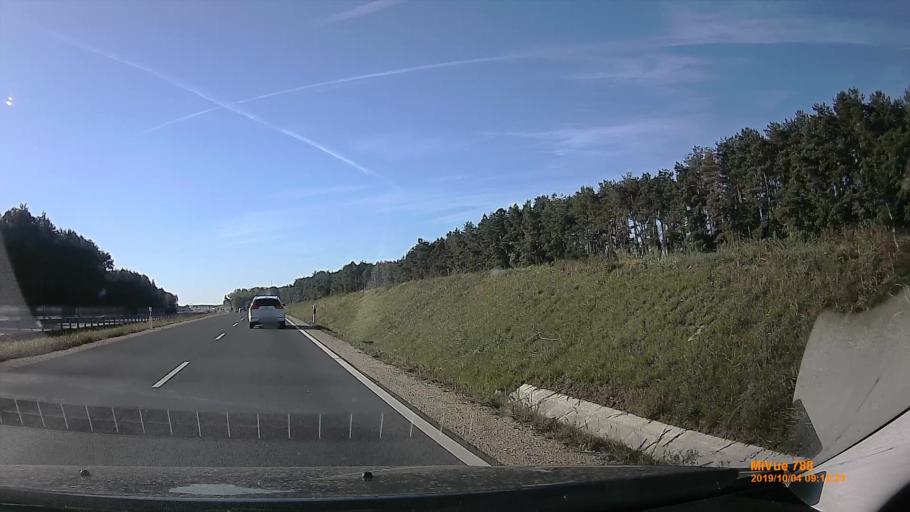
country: HU
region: Somogy
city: Karad
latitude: 46.6489
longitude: 17.7866
